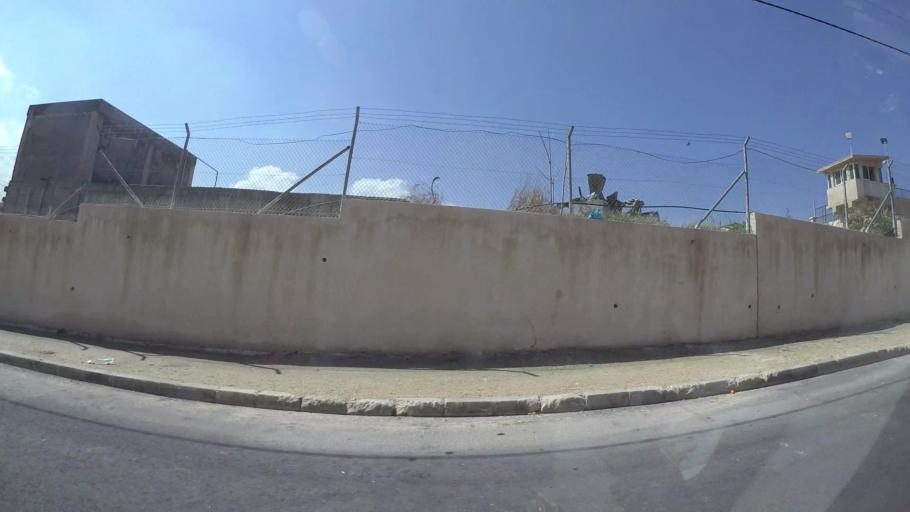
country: JO
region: Amman
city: Amman
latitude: 31.9759
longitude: 35.9862
